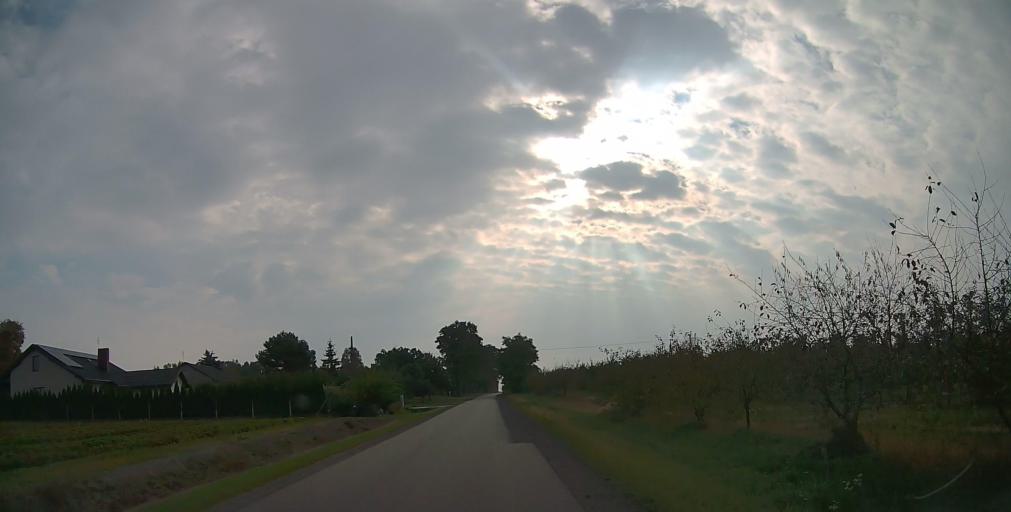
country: PL
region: Masovian Voivodeship
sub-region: Powiat grojecki
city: Mogielnica
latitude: 51.6574
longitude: 20.7164
